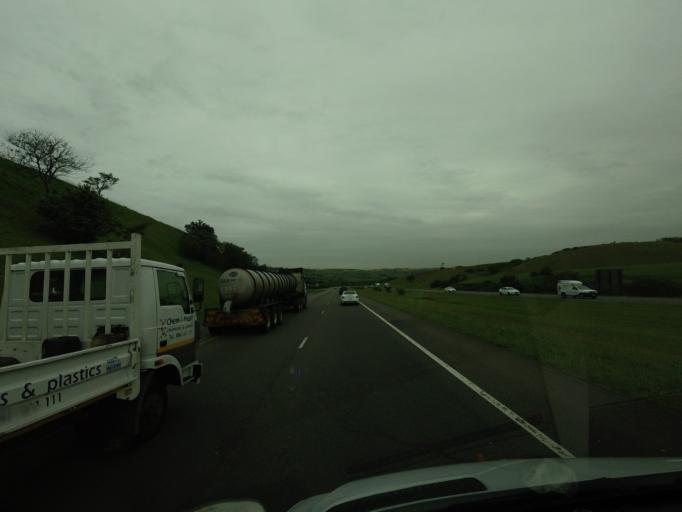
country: ZA
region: KwaZulu-Natal
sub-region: eThekwini Metropolitan Municipality
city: Durban
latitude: -29.6854
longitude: 31.0879
